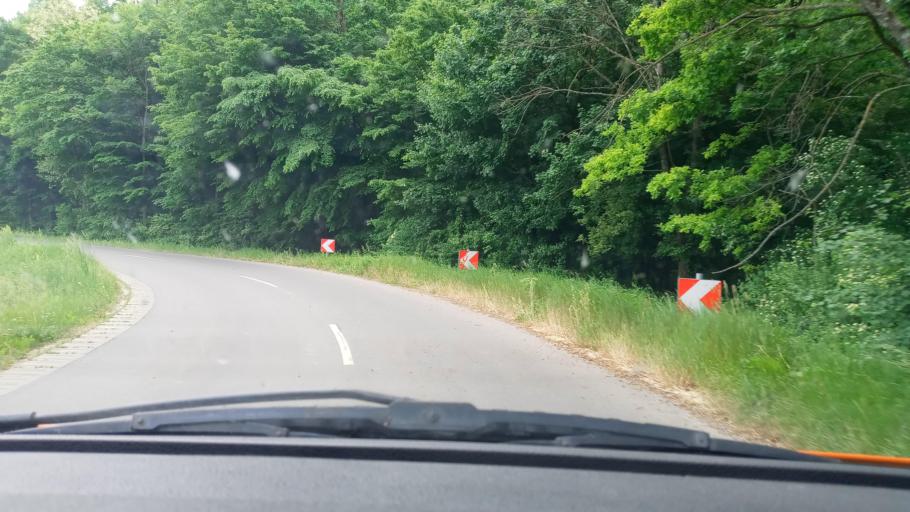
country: HU
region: Baranya
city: Vajszlo
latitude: 45.8403
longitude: 17.9743
